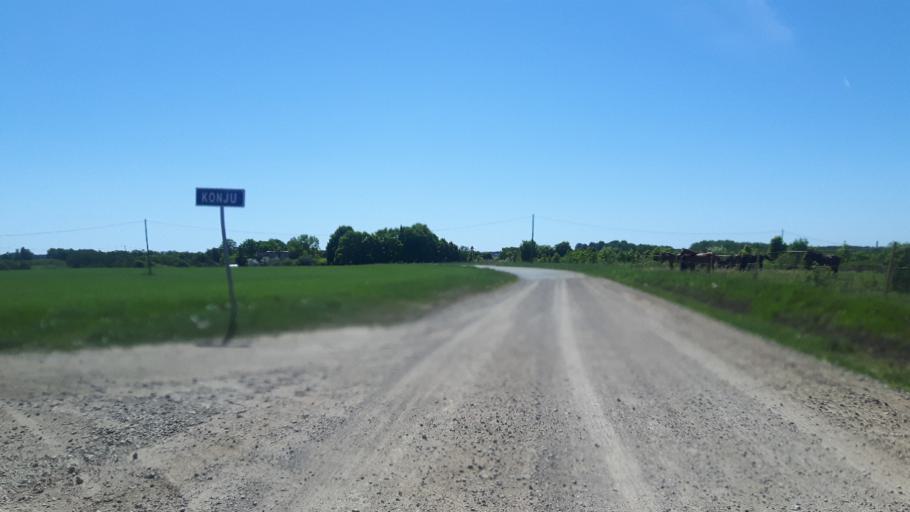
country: EE
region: Ida-Virumaa
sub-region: Toila vald
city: Voka
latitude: 59.4124
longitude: 27.6231
